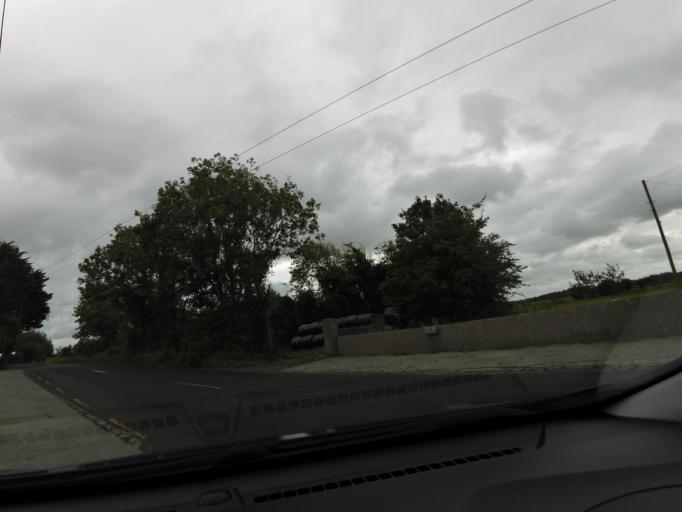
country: IE
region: Connaught
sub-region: County Galway
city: Loughrea
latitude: 53.2868
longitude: -8.5770
